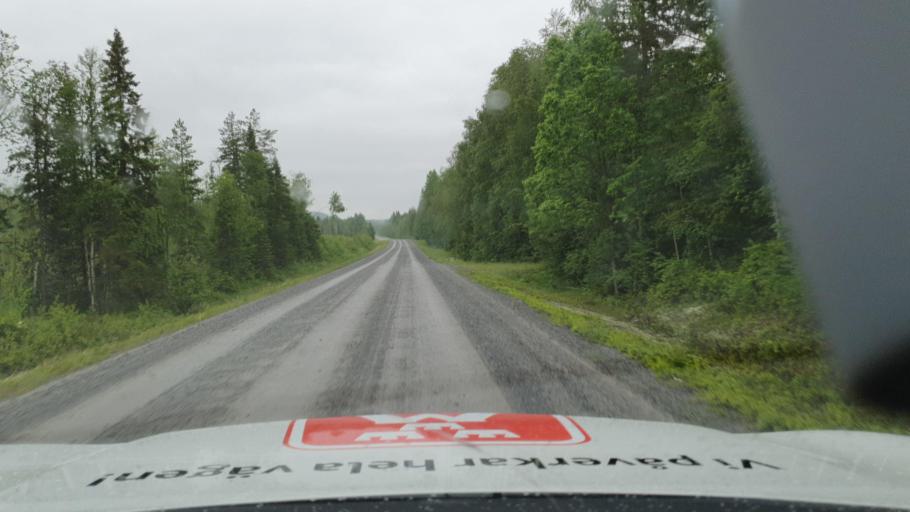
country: SE
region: Vaesterbotten
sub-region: Nordmalings Kommun
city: Nordmaling
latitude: 63.8347
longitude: 19.4858
